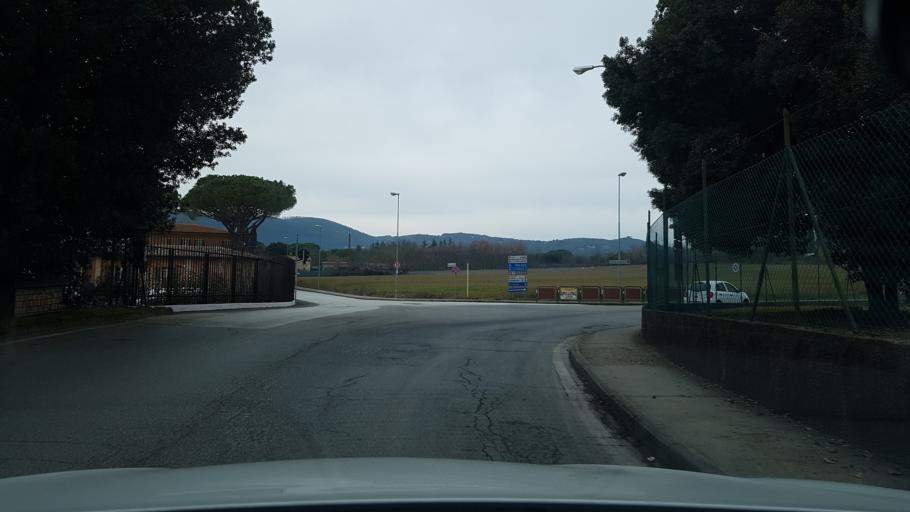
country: IT
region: Umbria
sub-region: Provincia di Perugia
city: Perugia
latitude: 43.1121
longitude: 12.3637
